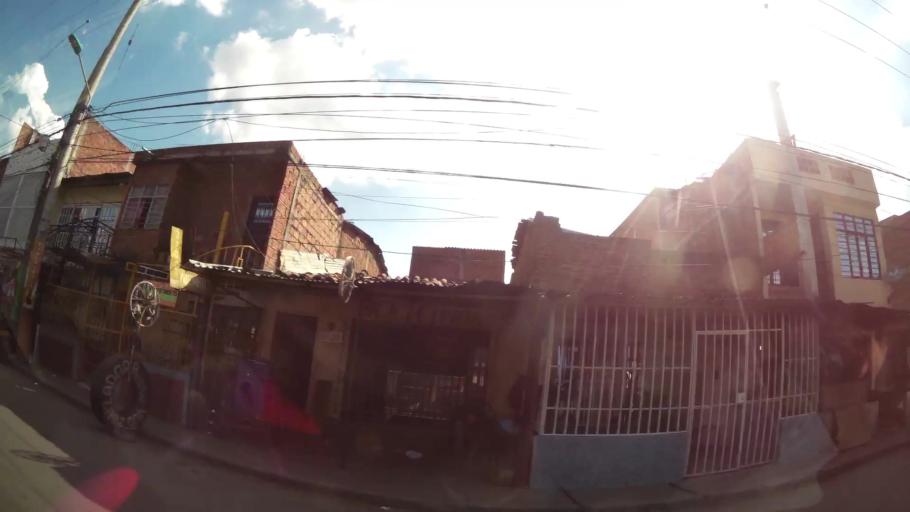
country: CO
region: Valle del Cauca
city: Cali
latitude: 3.4191
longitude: -76.4950
